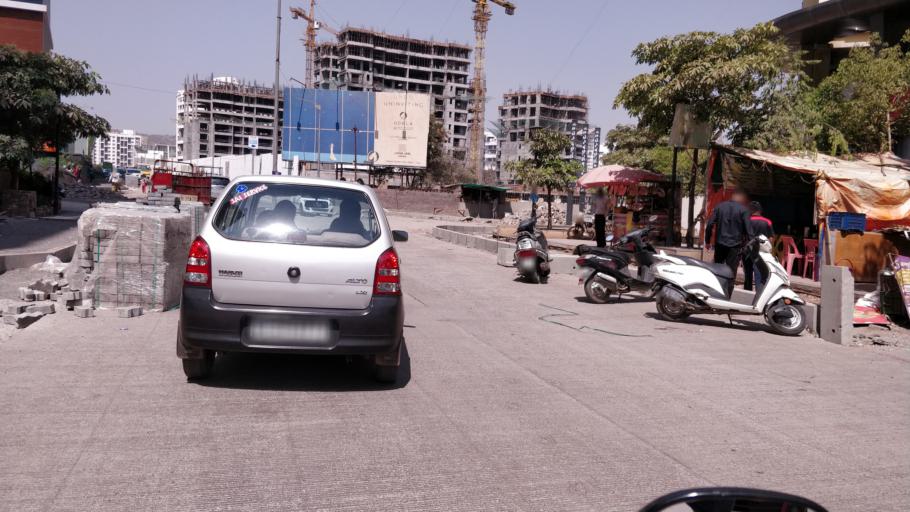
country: IN
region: Maharashtra
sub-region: Pune Division
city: Kharakvasla
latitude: 18.5114
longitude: 73.7754
